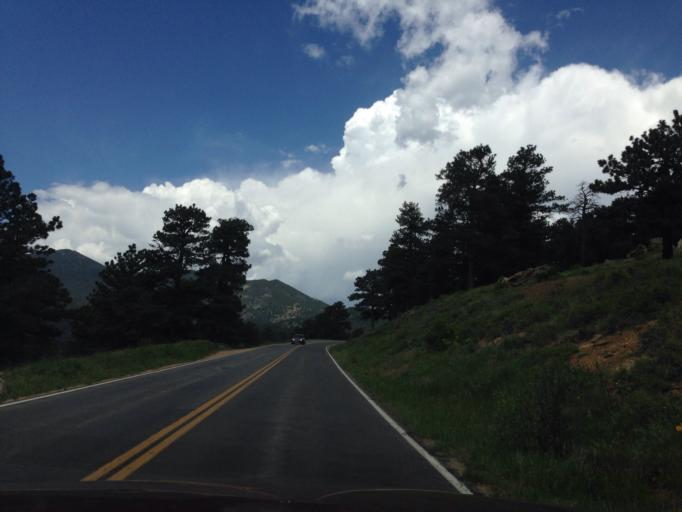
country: US
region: Colorado
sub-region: Larimer County
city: Estes Park
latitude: 40.3716
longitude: -105.5892
